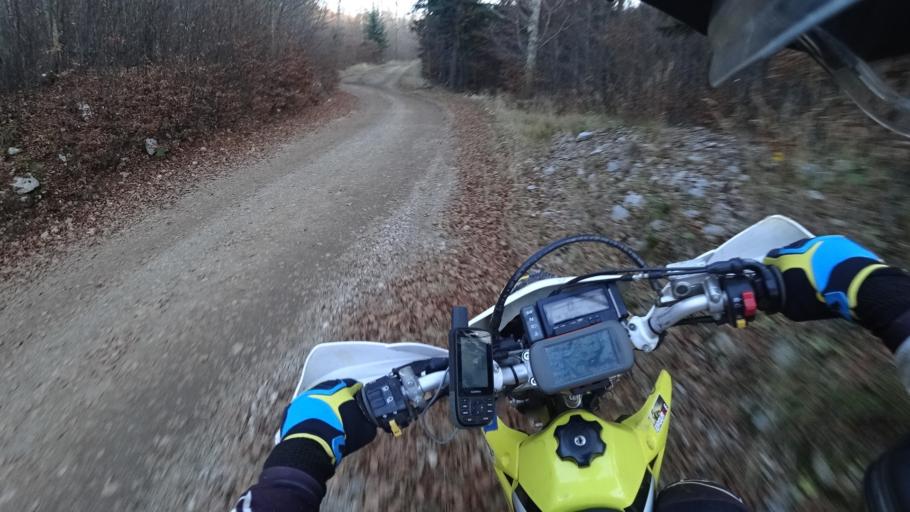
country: HR
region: Primorsko-Goranska
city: Drazice
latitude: 45.4880
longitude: 14.4812
